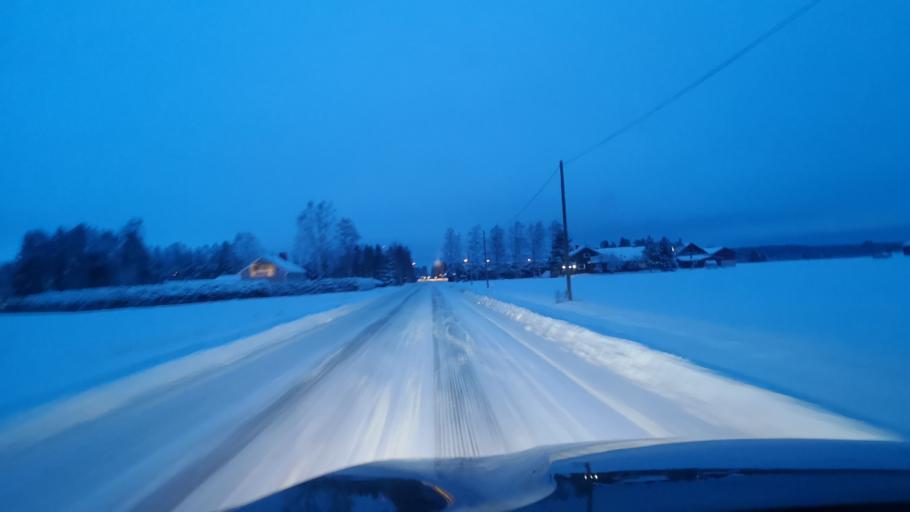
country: FI
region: Varsinais-Suomi
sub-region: Loimaa
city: Loimaa
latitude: 60.8811
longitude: 23.0891
